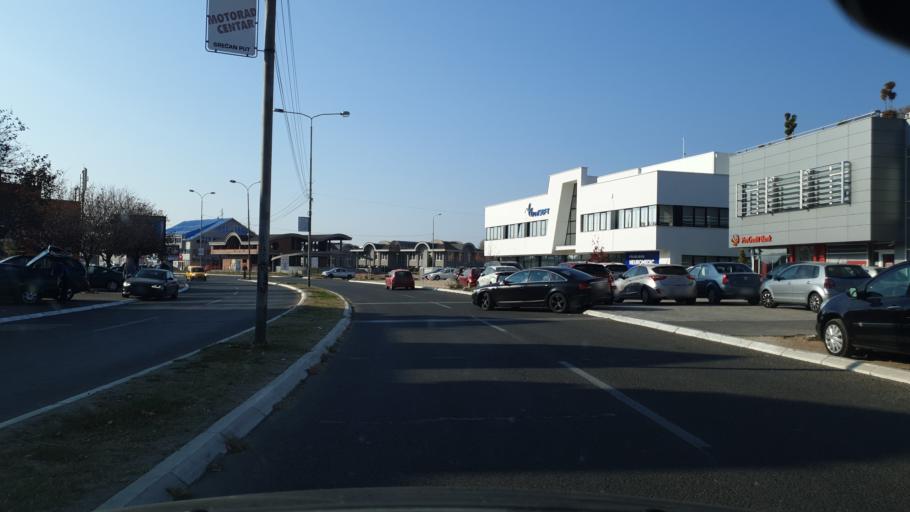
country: RS
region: Central Serbia
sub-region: Nisavski Okrug
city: Nis
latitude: 43.3237
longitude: 21.9308
